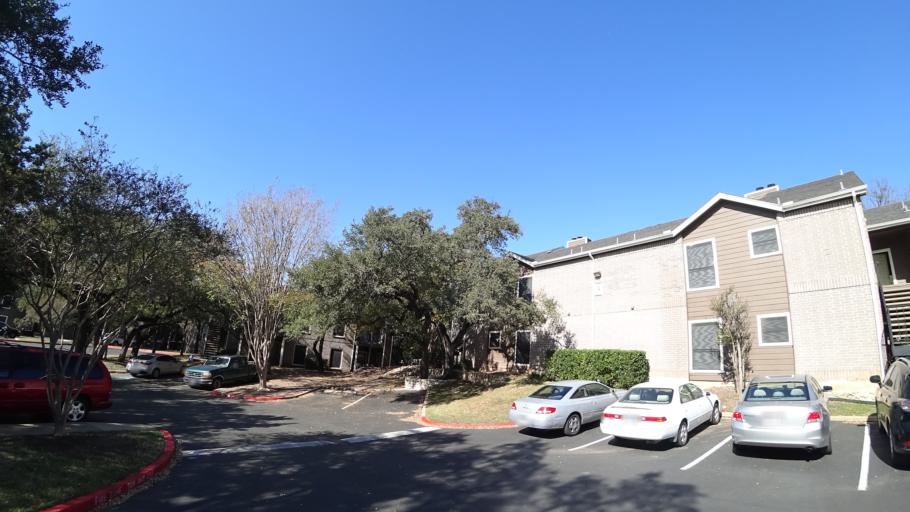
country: US
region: Texas
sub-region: Williamson County
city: Jollyville
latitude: 30.4115
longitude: -97.7491
